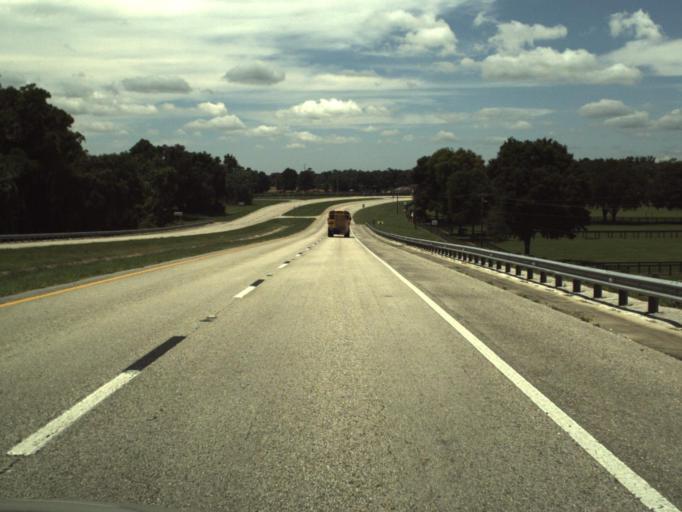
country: US
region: Florida
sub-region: Marion County
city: Citra
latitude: 29.3994
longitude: -82.2029
